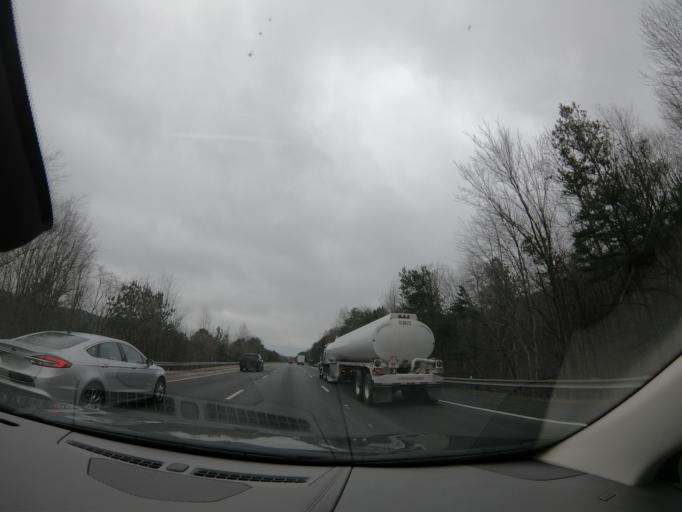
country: US
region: Georgia
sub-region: Whitfield County
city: Varnell
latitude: 34.8409
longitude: -85.0172
